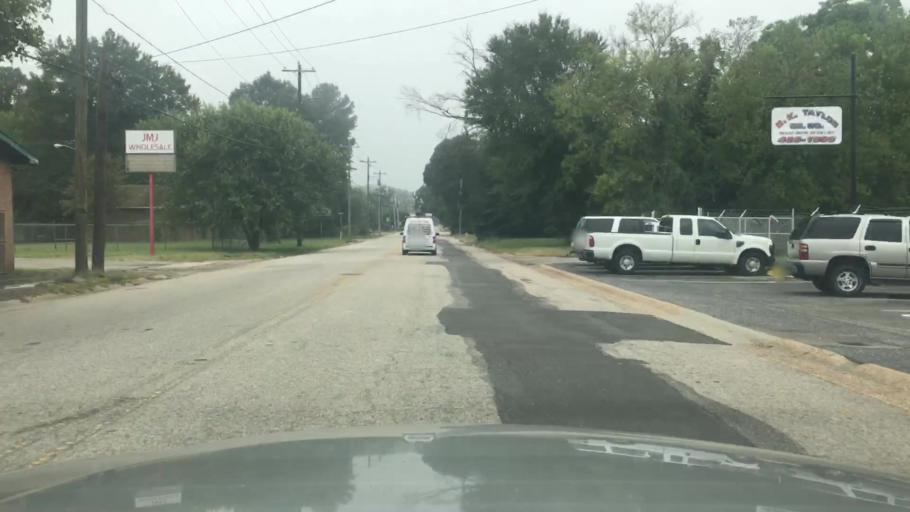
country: US
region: North Carolina
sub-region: Cumberland County
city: Fayetteville
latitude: 35.0652
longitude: -78.8799
